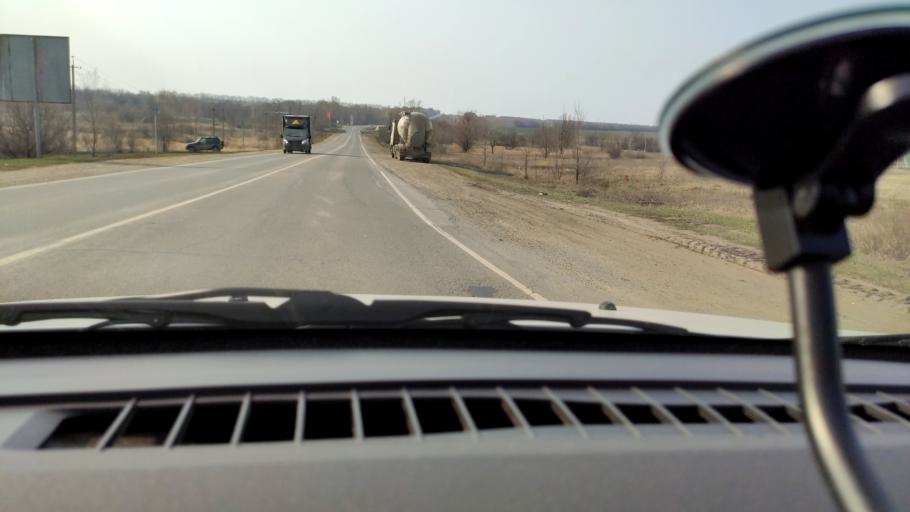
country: RU
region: Samara
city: Dubovyy Umet
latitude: 53.0633
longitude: 50.3749
